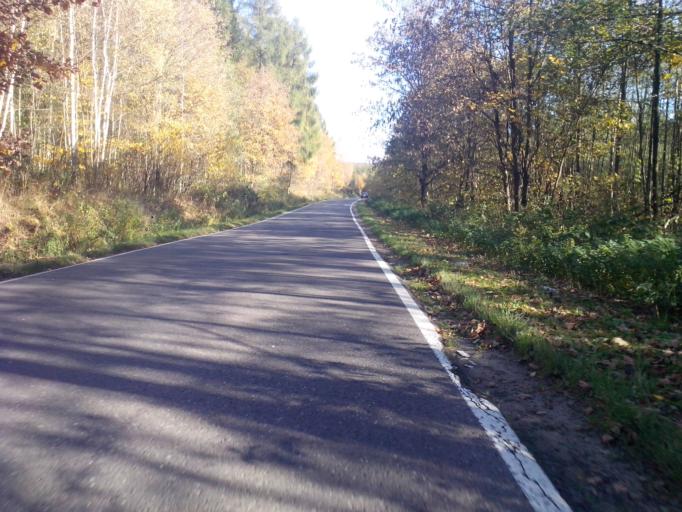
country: PL
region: Subcarpathian Voivodeship
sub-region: Powiat krosnienski
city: Korczyna
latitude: 49.7662
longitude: 21.8209
